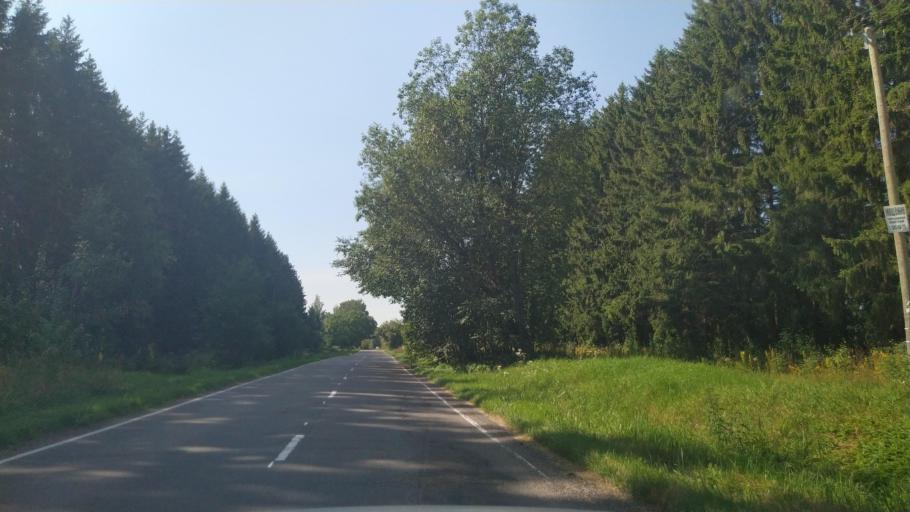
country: RU
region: Leningrad
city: Siverskiy
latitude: 59.3000
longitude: 30.0769
